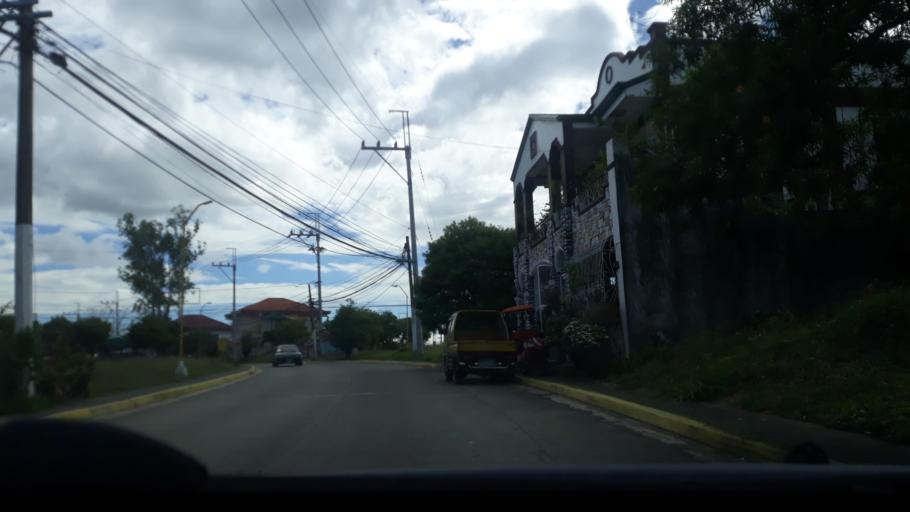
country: PH
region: Calabarzon
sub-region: Province of Cavite
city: Bulihan
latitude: 14.3038
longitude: 120.9689
